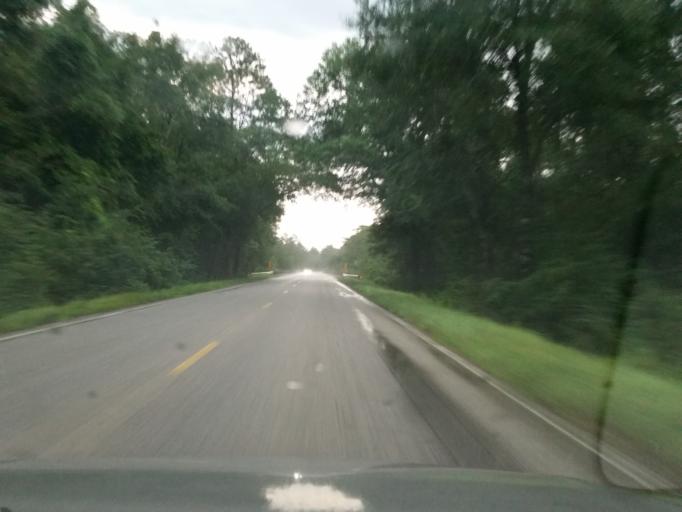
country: US
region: Florida
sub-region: Escambia County
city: Cantonment
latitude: 30.6050
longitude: -87.4056
